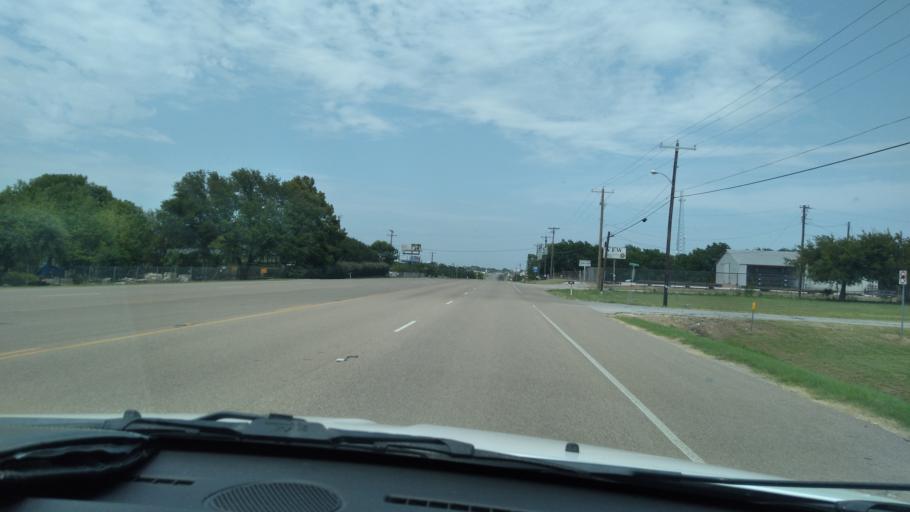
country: US
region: Texas
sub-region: Navarro County
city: Corsicana
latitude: 32.0606
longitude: -96.5199
